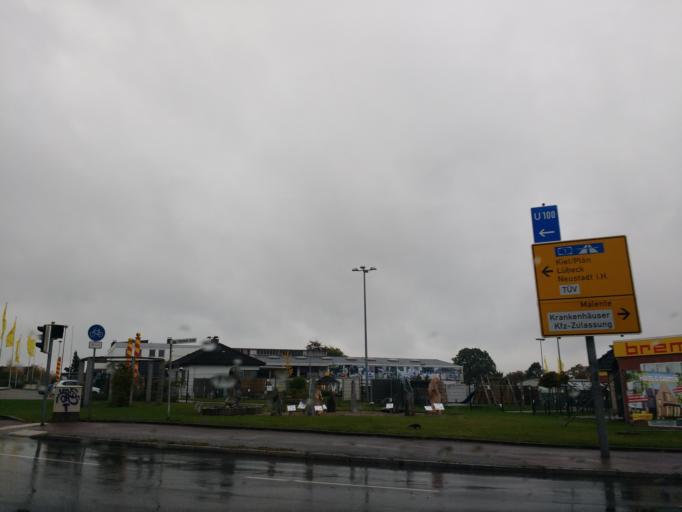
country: DE
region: Schleswig-Holstein
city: Eutin
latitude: 54.1287
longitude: 10.6255
